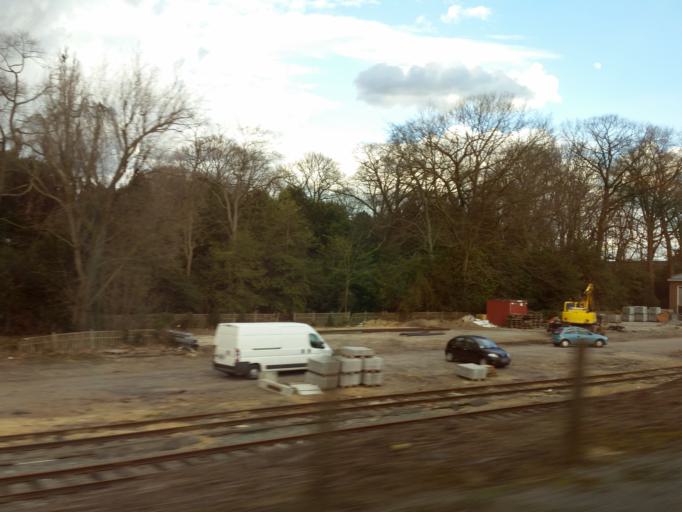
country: BE
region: Flanders
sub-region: Provincie Oost-Vlaanderen
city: Melle
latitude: 51.0034
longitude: 3.7961
